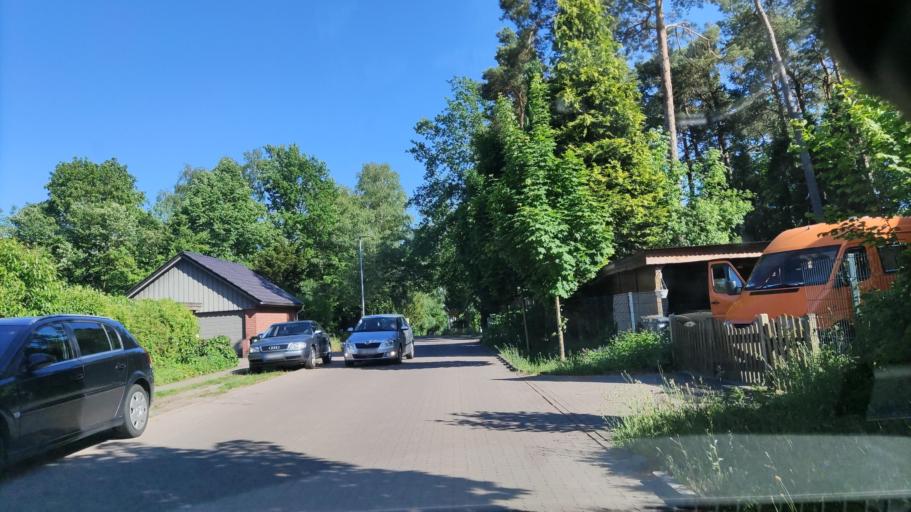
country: DE
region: Lower Saxony
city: Harmstorf
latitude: 53.3748
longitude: 10.0386
